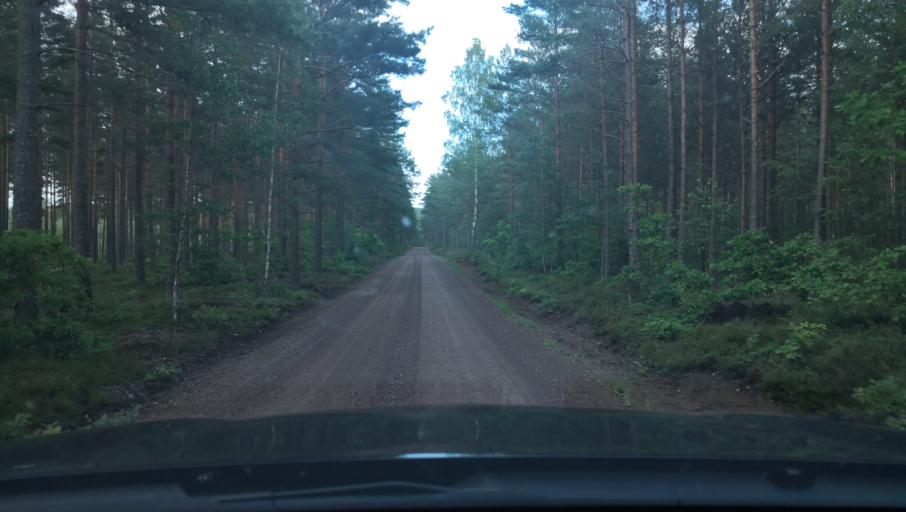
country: SE
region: Kalmar
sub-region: Hultsfreds Kommun
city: Malilla
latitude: 57.3912
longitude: 15.7530
